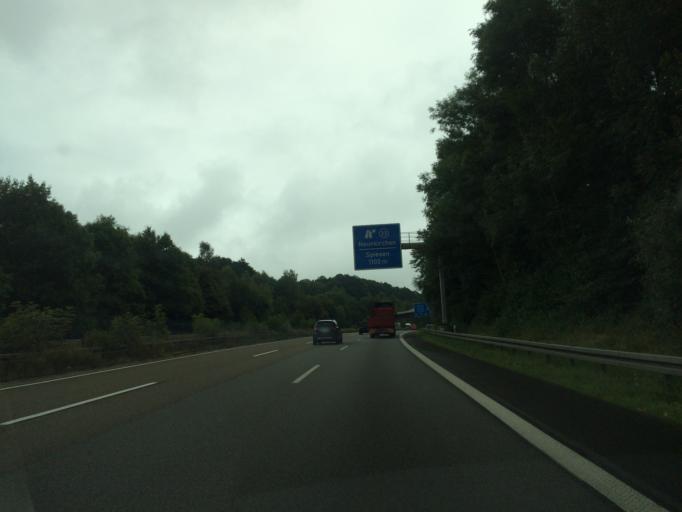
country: DE
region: Saarland
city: Spiesen-Elversberg
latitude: 49.3239
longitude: 7.1307
